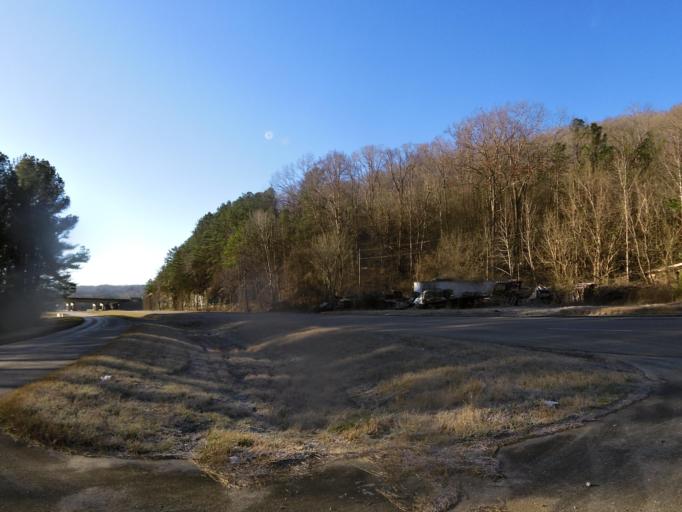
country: US
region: Alabama
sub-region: Morgan County
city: Falkville
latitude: 34.3195
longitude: -86.9018
